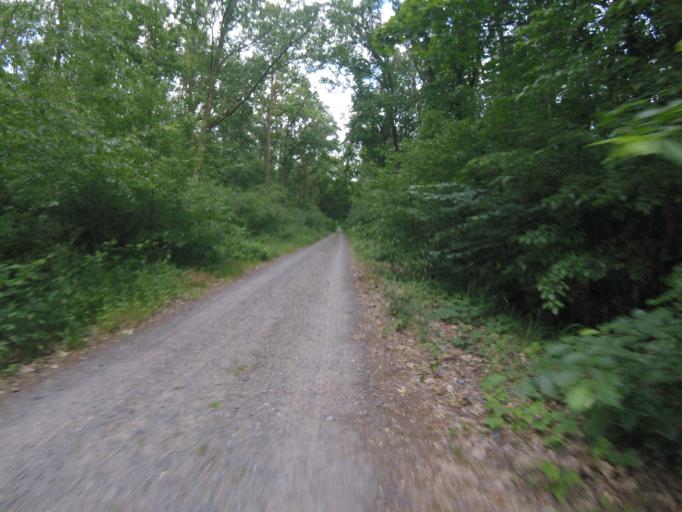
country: DE
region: Brandenburg
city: Konigs Wusterhausen
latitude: 52.3069
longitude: 13.6083
